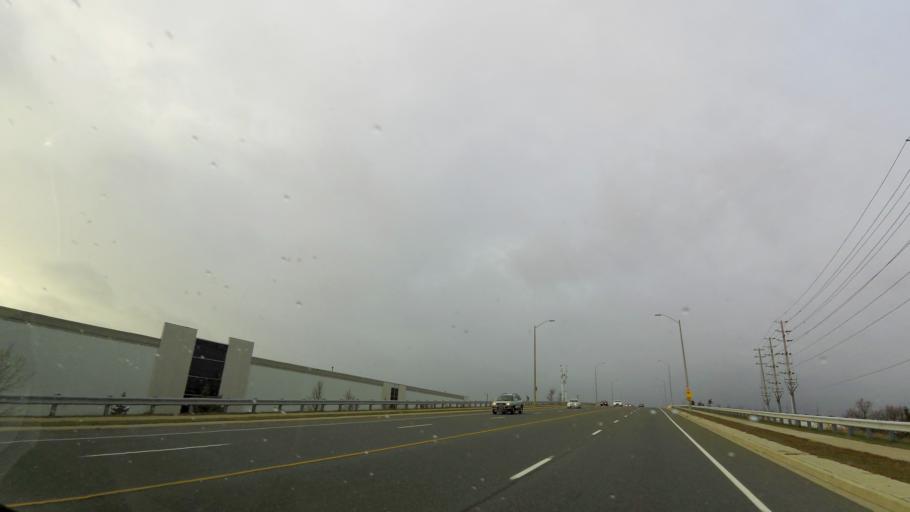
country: CA
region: Ontario
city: Mississauga
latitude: 43.6223
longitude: -79.6974
